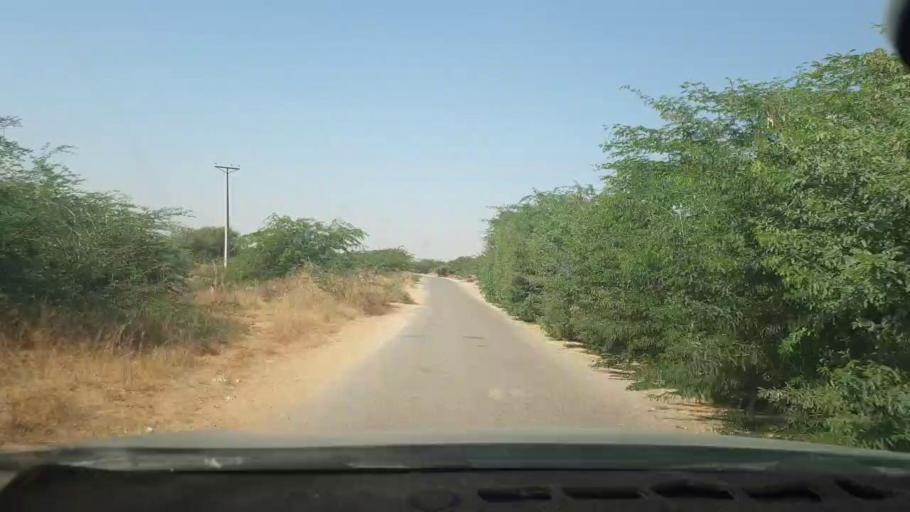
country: PK
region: Sindh
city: Malir Cantonment
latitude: 25.1570
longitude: 67.1436
